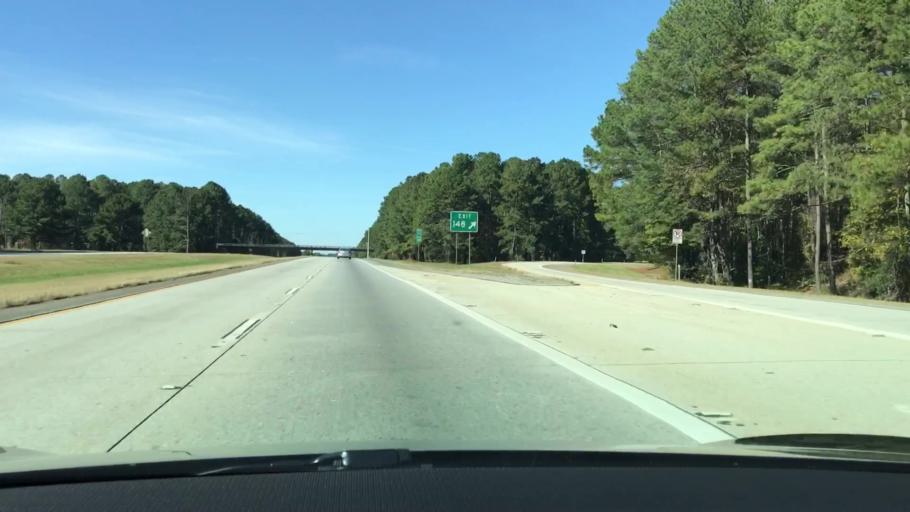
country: US
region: Georgia
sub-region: Taliaferro County
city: Crawfordville
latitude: 33.5298
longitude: -82.9059
